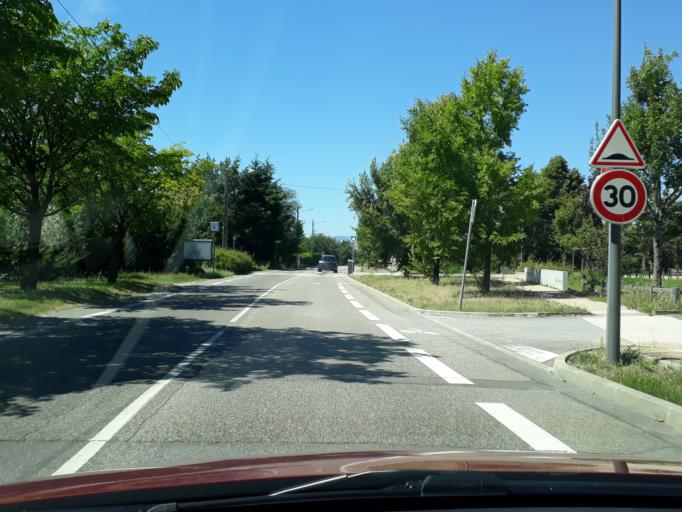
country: FR
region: Rhone-Alpes
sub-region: Departement du Rhone
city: Saint-Priest
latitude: 45.6923
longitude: 4.9625
